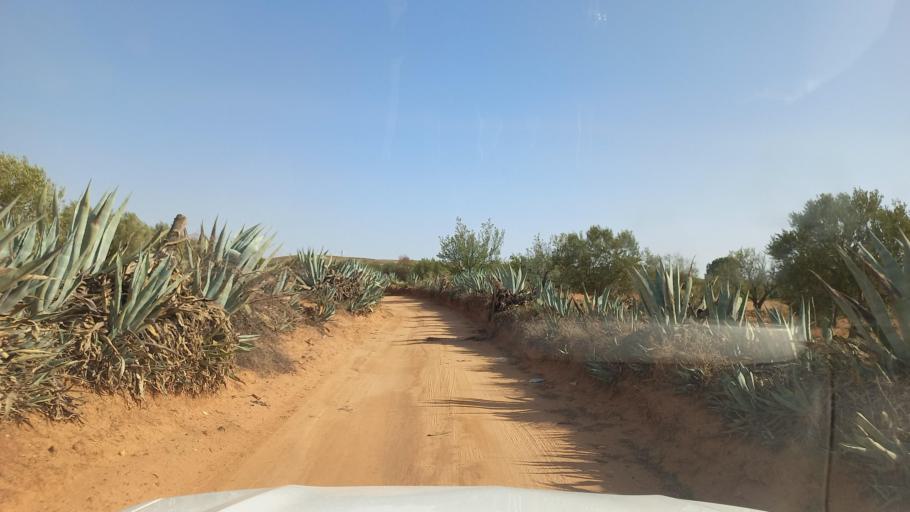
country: TN
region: Al Qasrayn
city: Kasserine
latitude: 35.2030
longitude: 8.9630
